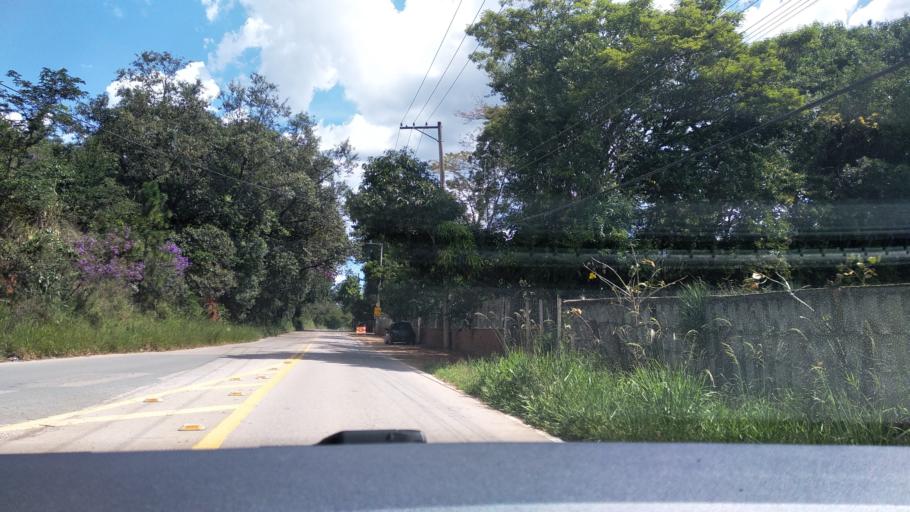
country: BR
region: Sao Paulo
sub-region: Varzea Paulista
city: Varzea Paulista
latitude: -23.2407
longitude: -46.8716
